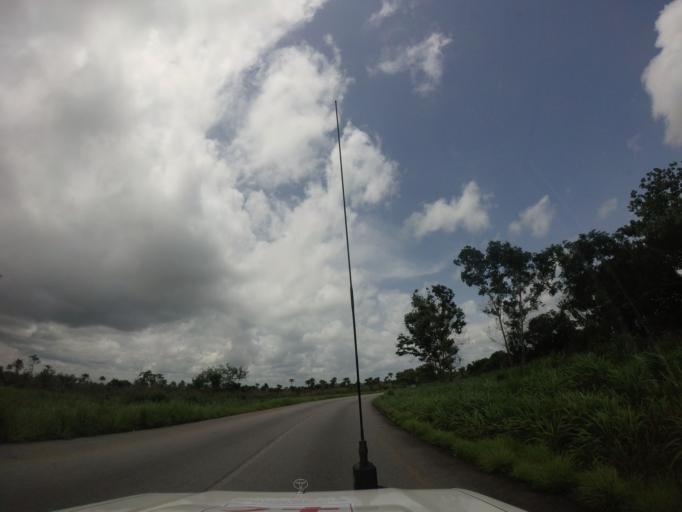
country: SL
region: Northern Province
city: Lunsar
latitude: 8.4754
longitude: -12.5360
